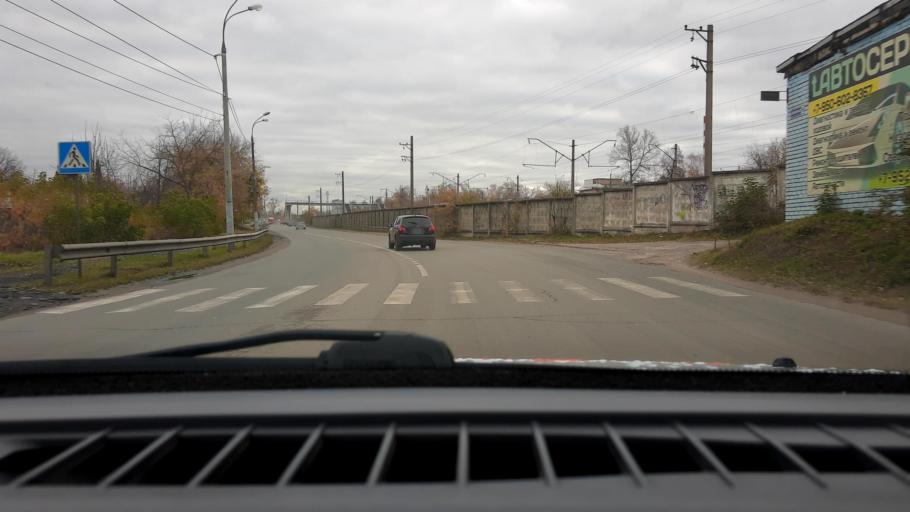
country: RU
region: Nizjnij Novgorod
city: Gorbatovka
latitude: 56.3688
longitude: 43.8280
